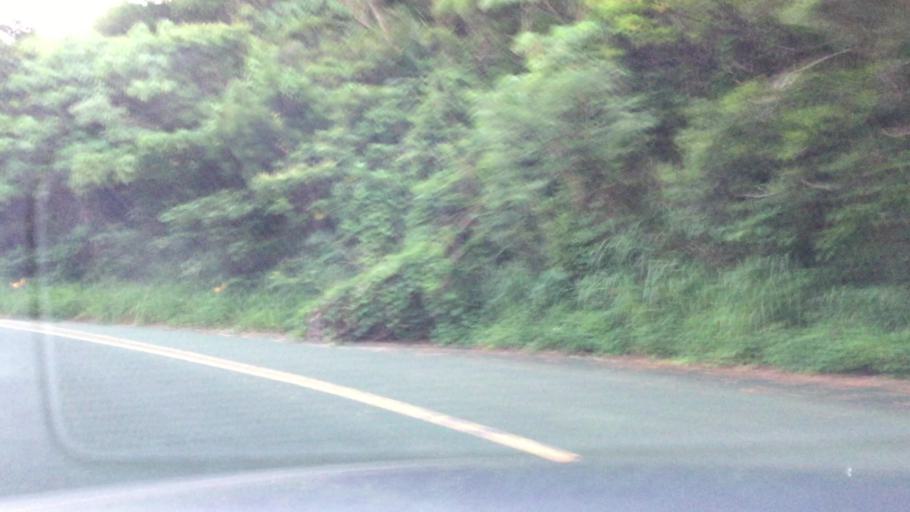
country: JP
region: Okinawa
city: Ishigaki
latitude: 24.3695
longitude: 124.1602
